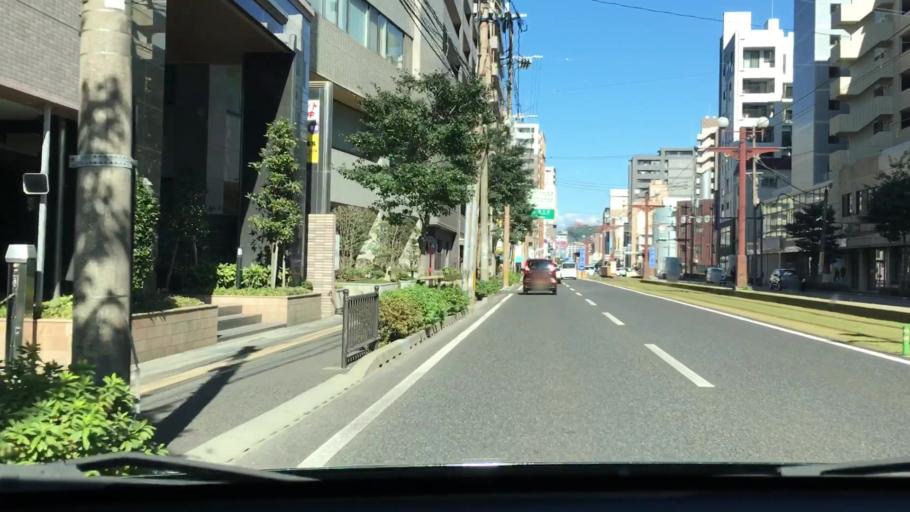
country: JP
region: Kagoshima
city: Kagoshima-shi
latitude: 31.5774
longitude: 130.5424
